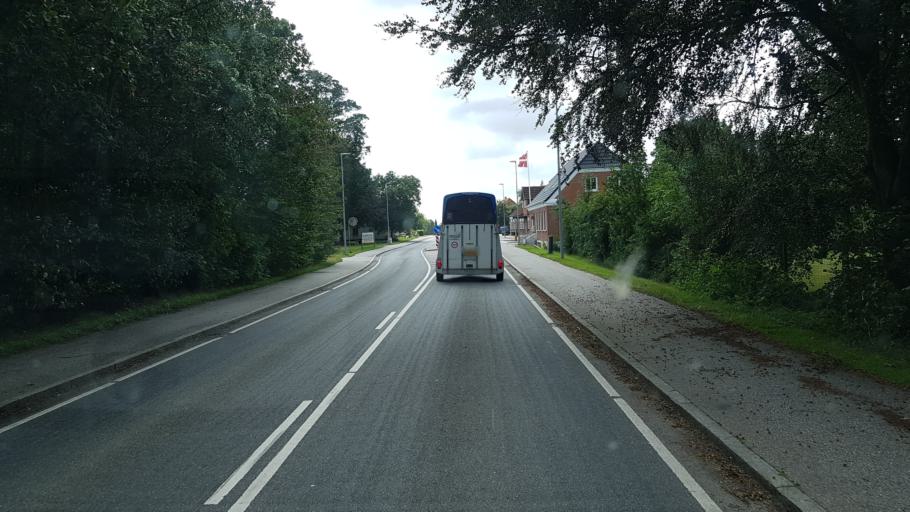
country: DK
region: South Denmark
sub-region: Vejen Kommune
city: Brorup
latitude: 55.5170
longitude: 9.0265
